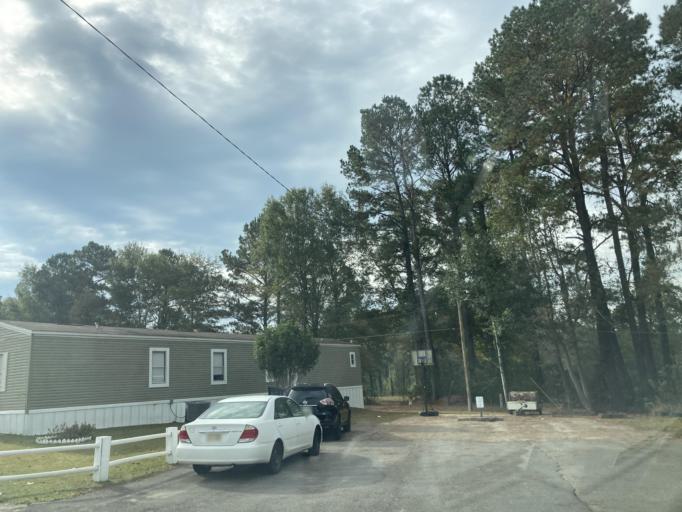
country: US
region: Mississippi
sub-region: Lamar County
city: West Hattiesburg
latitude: 31.3042
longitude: -89.3785
